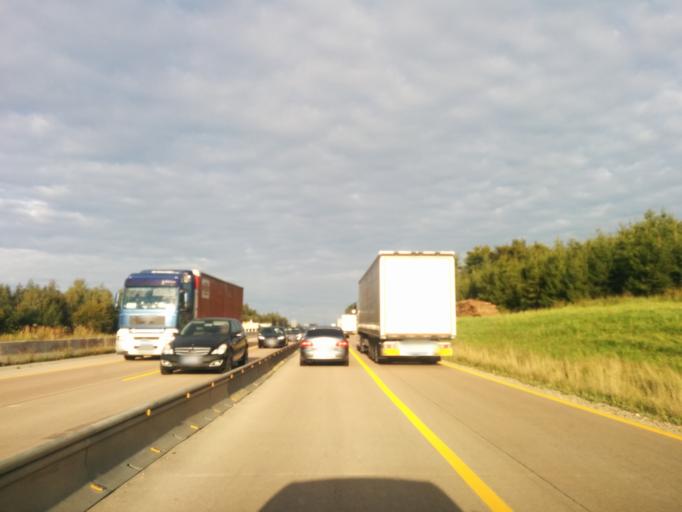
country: DE
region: Bavaria
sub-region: Swabia
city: Aystetten
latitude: 48.4182
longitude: 10.7634
